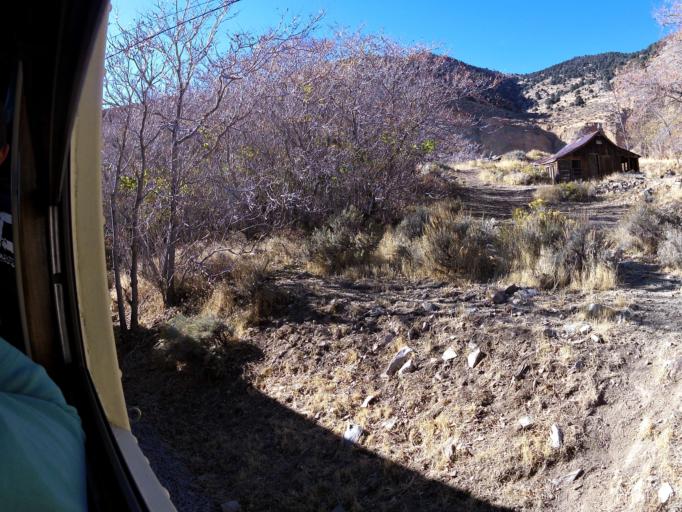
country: US
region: Nevada
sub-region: Storey County
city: Virginia City
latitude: 39.2943
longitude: -119.6570
